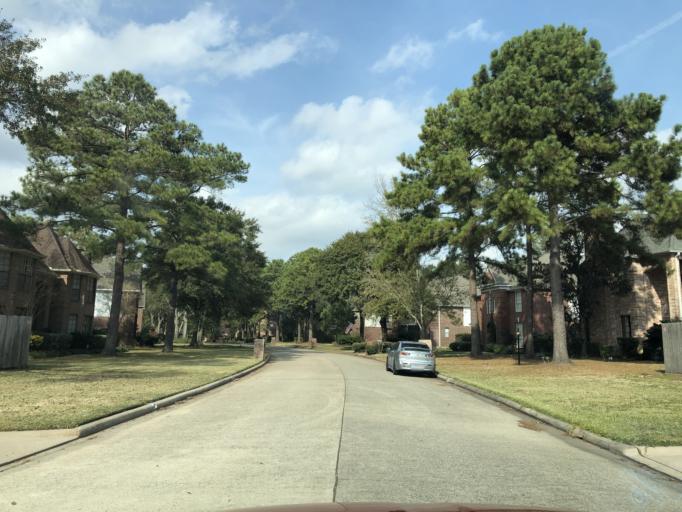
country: US
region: Texas
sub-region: Harris County
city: Tomball
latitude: 30.0224
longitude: -95.5444
